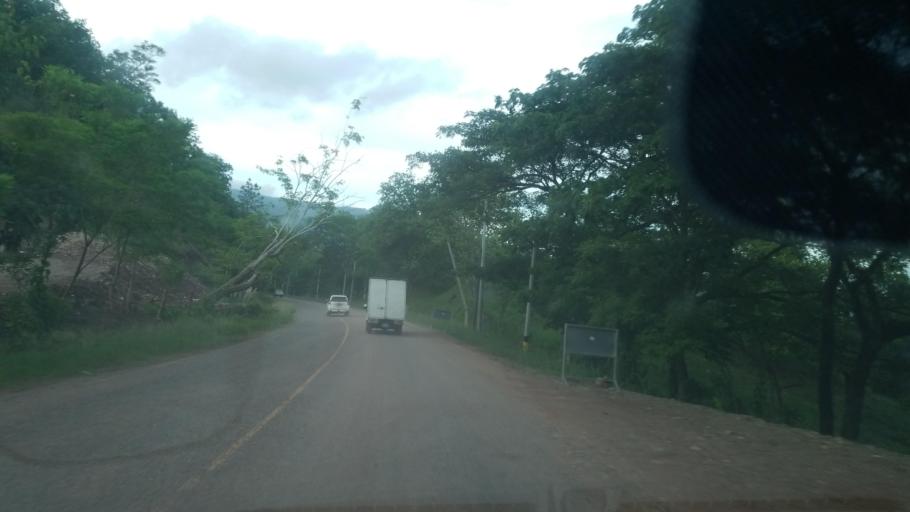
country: HN
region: Santa Barbara
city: Concepcion del Sur
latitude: 14.7988
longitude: -88.1489
